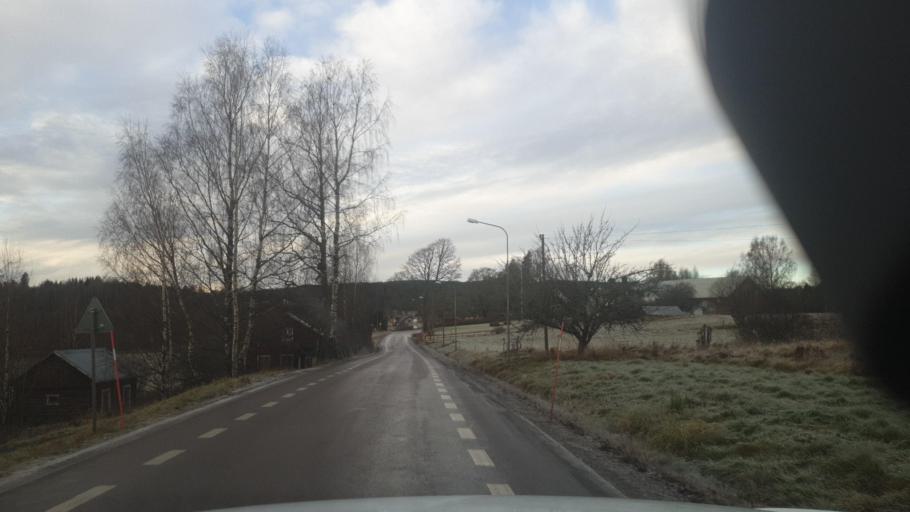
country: SE
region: Vaermland
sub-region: Arvika Kommun
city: Arvika
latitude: 59.8141
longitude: 12.5710
